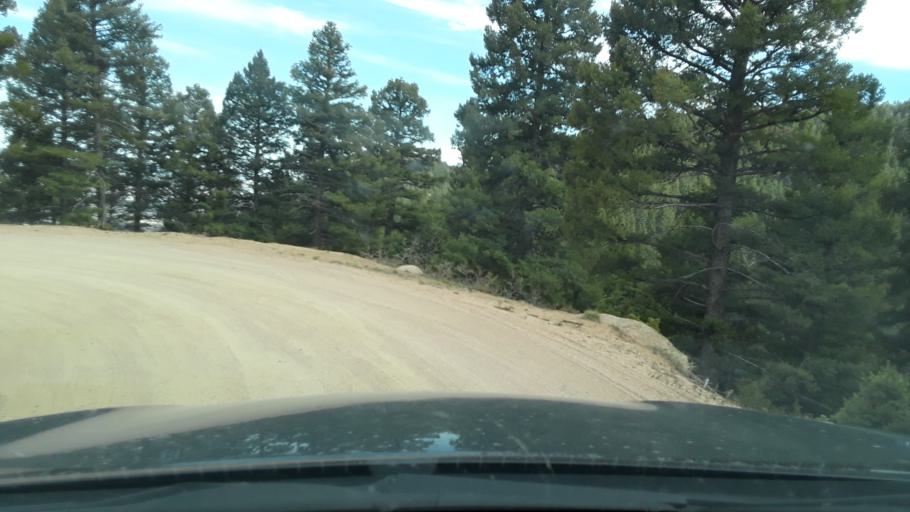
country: US
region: Colorado
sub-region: El Paso County
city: Palmer Lake
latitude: 39.0697
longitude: -104.9346
